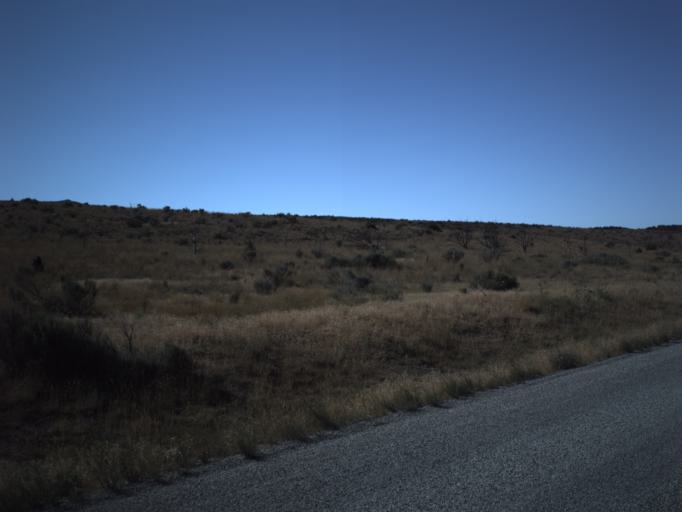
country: US
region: Utah
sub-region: Juab County
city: Mona
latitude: 39.7926
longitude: -112.1481
